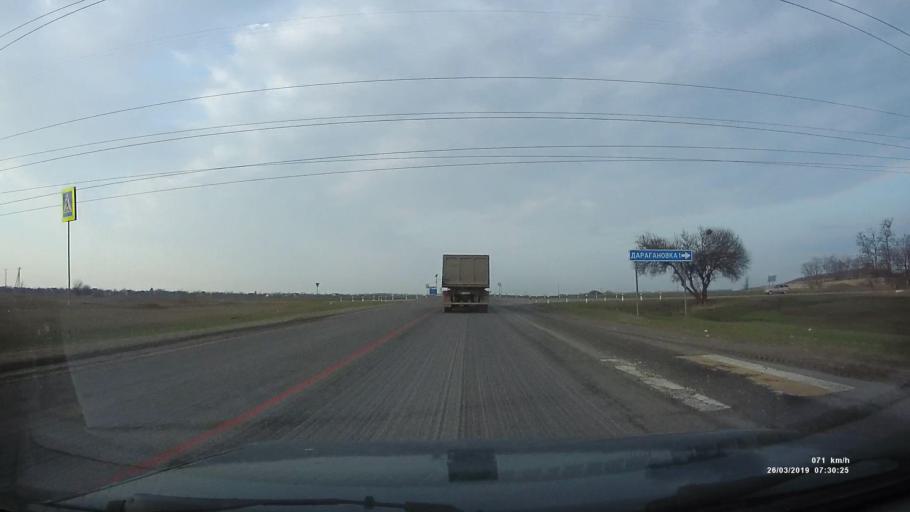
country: RU
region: Rostov
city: Novobessergenovka
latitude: 47.2369
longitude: 38.8069
